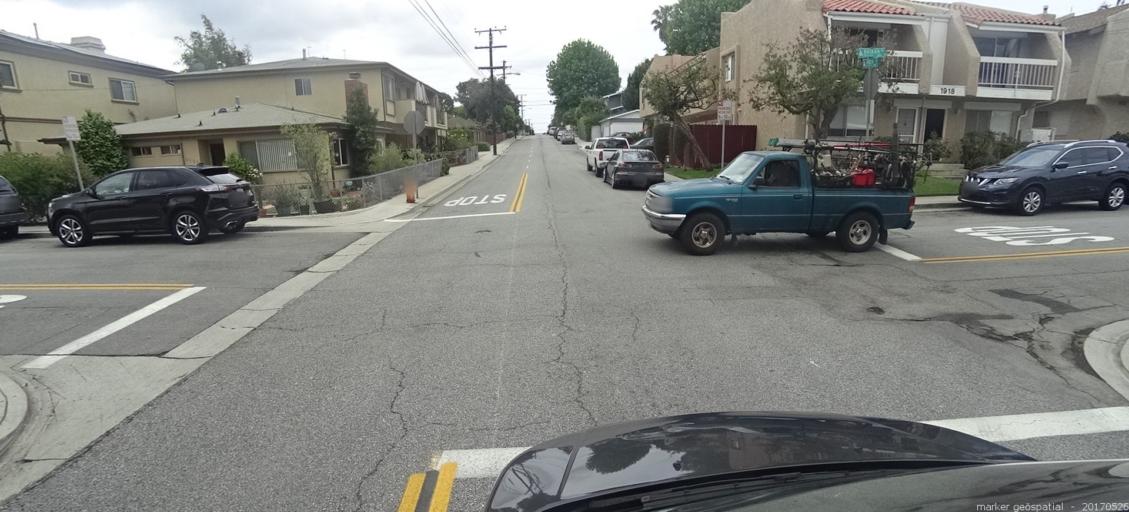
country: US
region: California
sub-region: Los Angeles County
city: Lawndale
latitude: 33.8848
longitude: -118.3770
